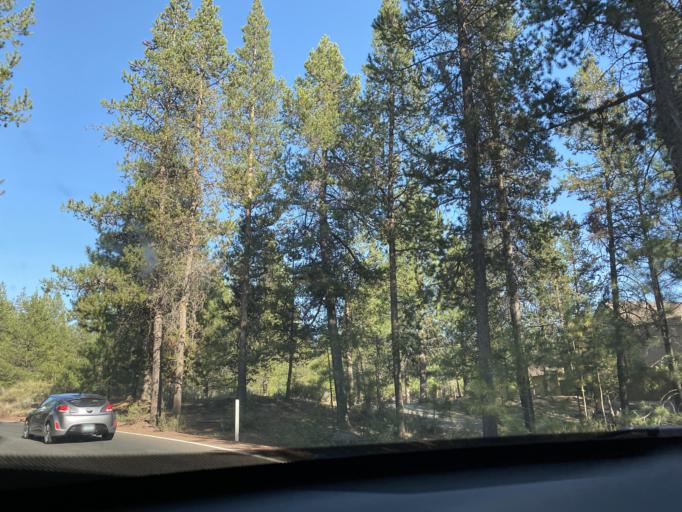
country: US
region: Oregon
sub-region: Deschutes County
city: Sunriver
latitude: 43.8783
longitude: -121.4351
